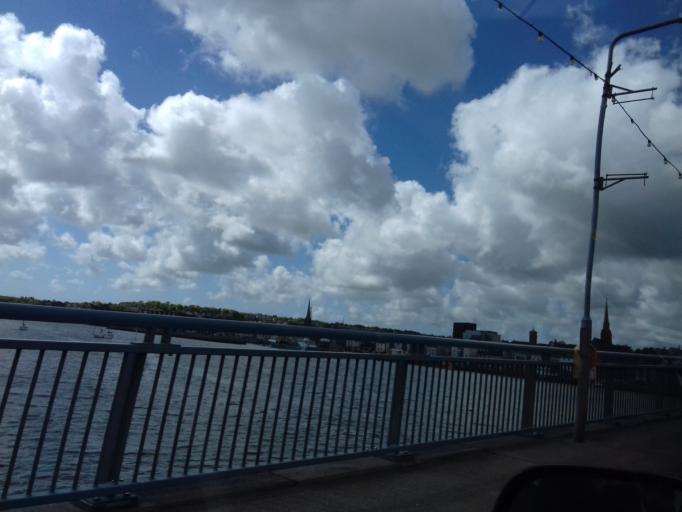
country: IE
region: Leinster
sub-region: Loch Garman
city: Loch Garman
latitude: 52.3431
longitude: -6.4572
